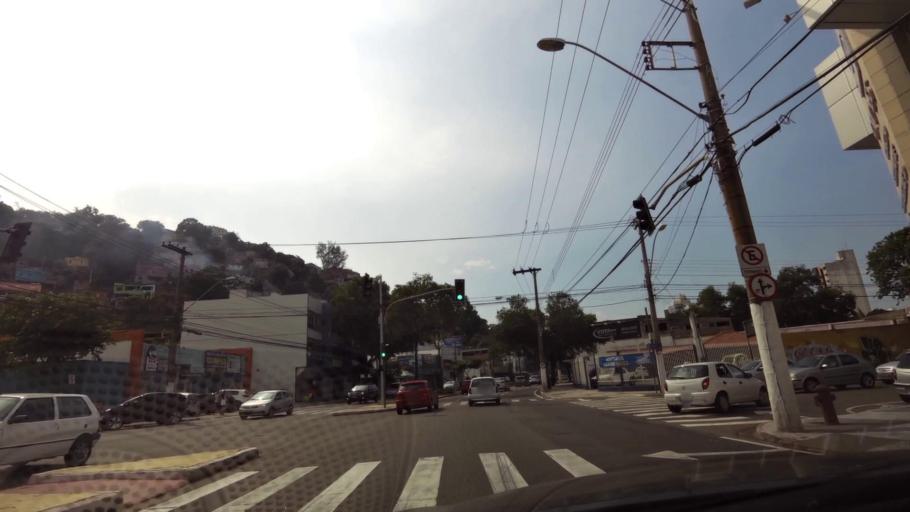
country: BR
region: Espirito Santo
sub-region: Vila Velha
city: Vila Velha
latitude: -20.3100
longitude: -40.3088
